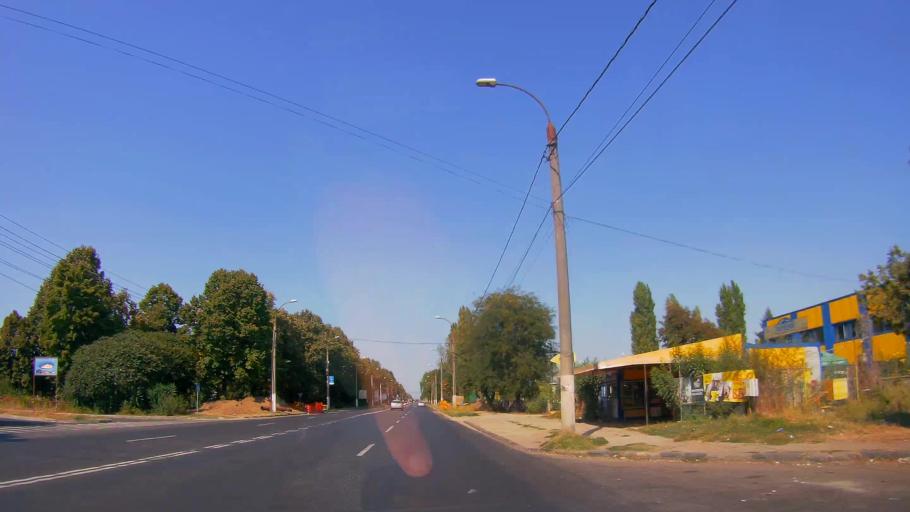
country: RO
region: Giurgiu
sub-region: Comuna Fratesti
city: Remus
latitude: 43.9218
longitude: 25.9736
